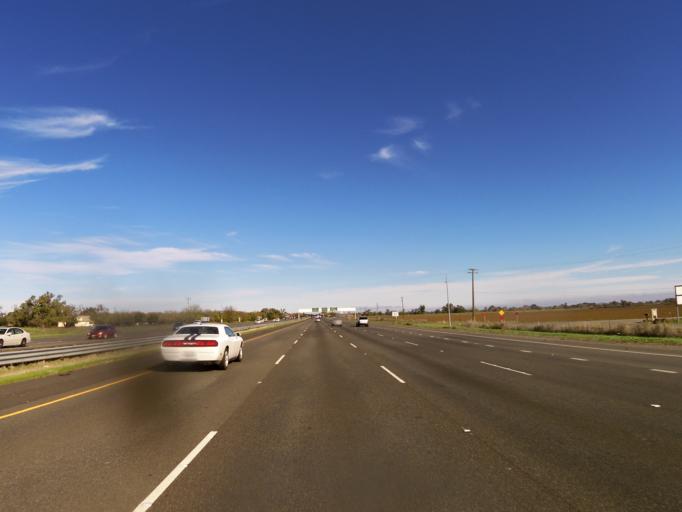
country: US
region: California
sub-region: Yolo County
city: Davis
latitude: 38.5118
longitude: -121.7785
